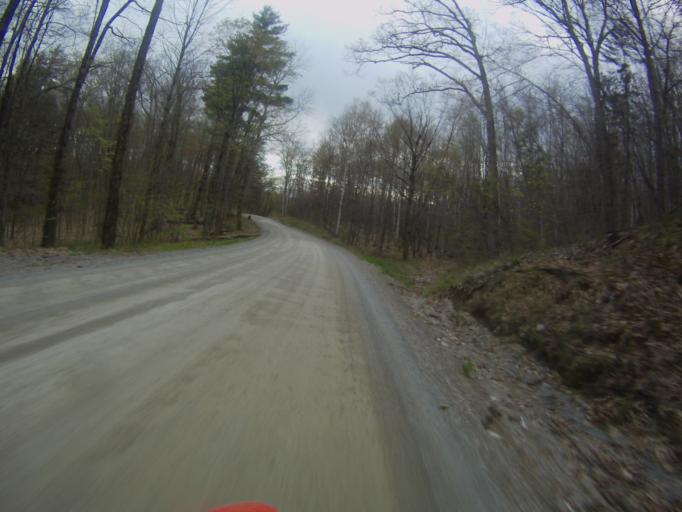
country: US
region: Vermont
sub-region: Addison County
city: Middlebury (village)
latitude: 43.9734
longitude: -73.0809
